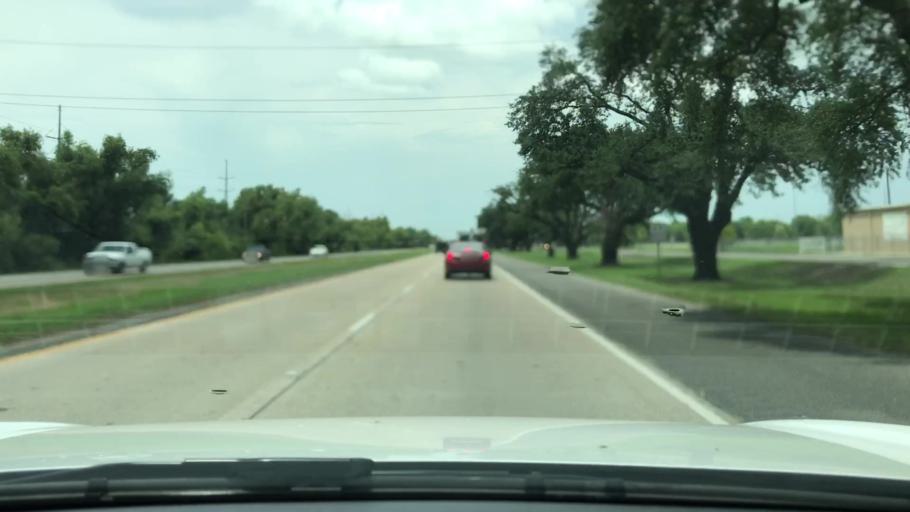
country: US
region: Louisiana
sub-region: West Baton Rouge Parish
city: Addis
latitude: 30.3237
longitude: -91.2530
